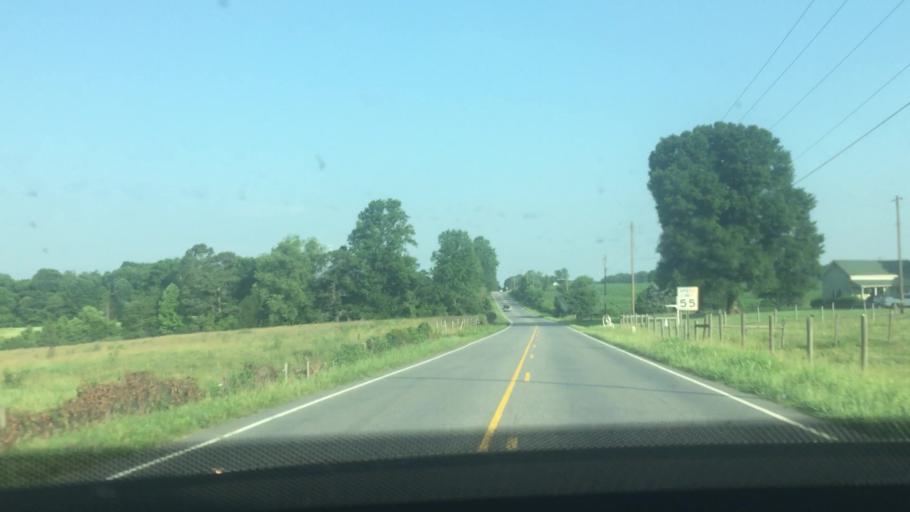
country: US
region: North Carolina
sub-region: Iredell County
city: Mooresville
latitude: 35.5896
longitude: -80.7512
